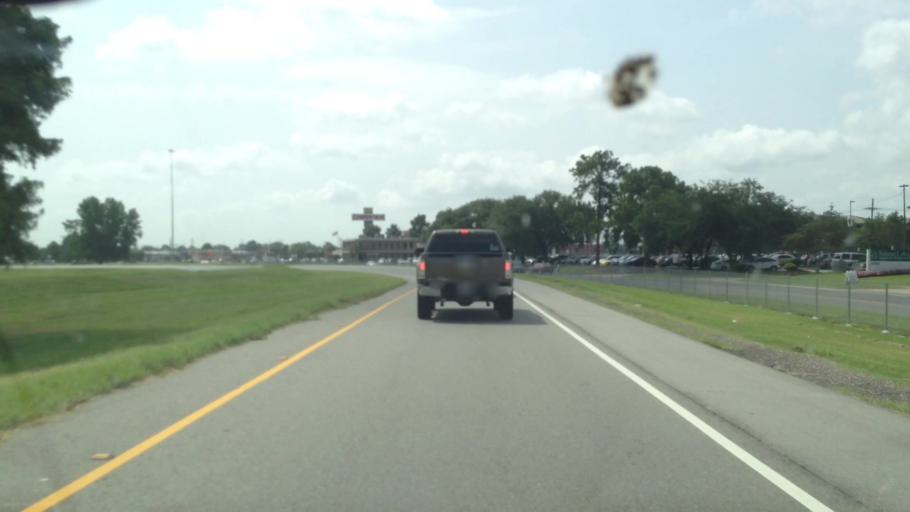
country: US
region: Louisiana
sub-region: Jefferson Parish
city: Metairie Terrace
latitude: 29.9986
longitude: -90.1862
